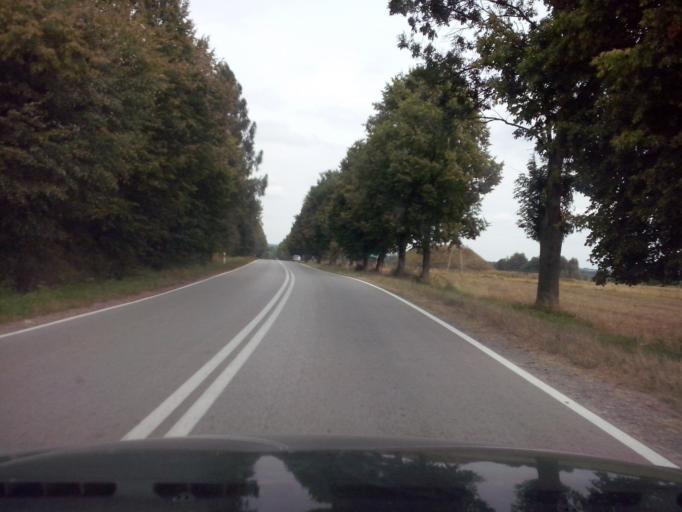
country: PL
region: Swietokrzyskie
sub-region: Powiat kielecki
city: Rakow
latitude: 50.6900
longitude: 21.0592
